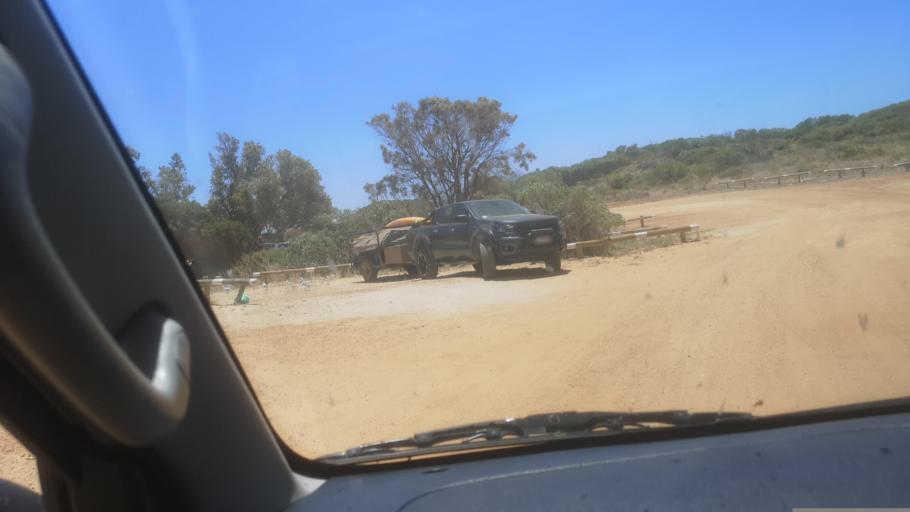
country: AU
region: Western Australia
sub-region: Dandaragan
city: Jurien Bay
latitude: -30.1820
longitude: 114.9998
